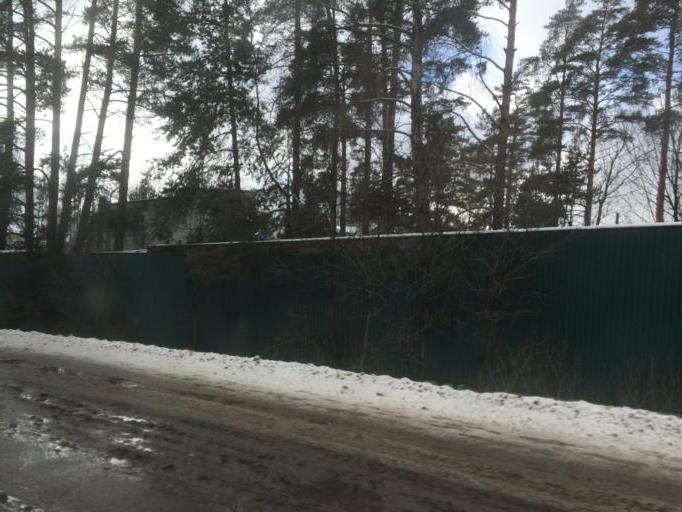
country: RU
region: Moskovskaya
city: Pavlovskaya Sloboda
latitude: 55.8051
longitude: 37.1270
